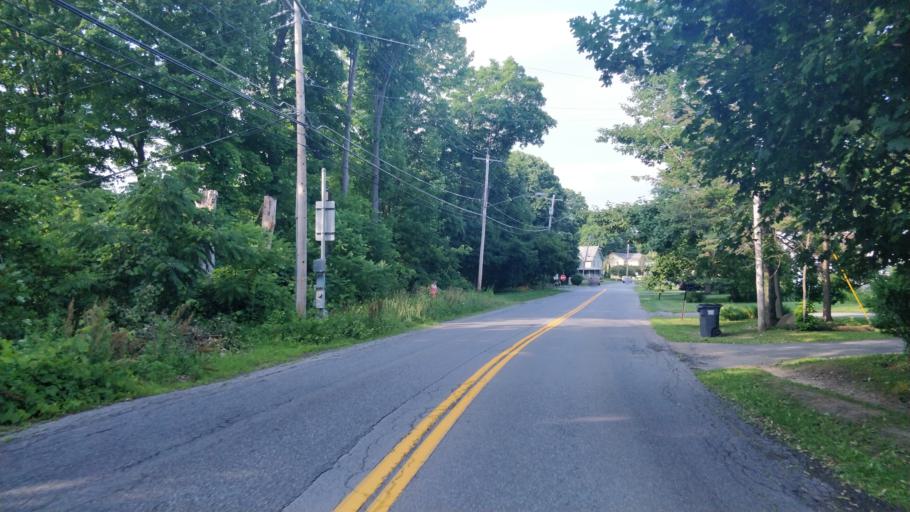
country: US
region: New York
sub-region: Saratoga County
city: Ballston Spa
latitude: 43.0082
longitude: -73.8438
